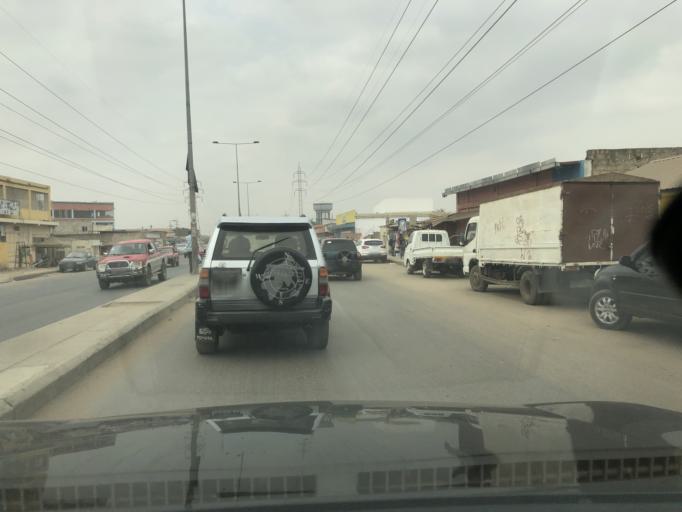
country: AO
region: Luanda
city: Luanda
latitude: -8.8178
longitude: 13.2793
